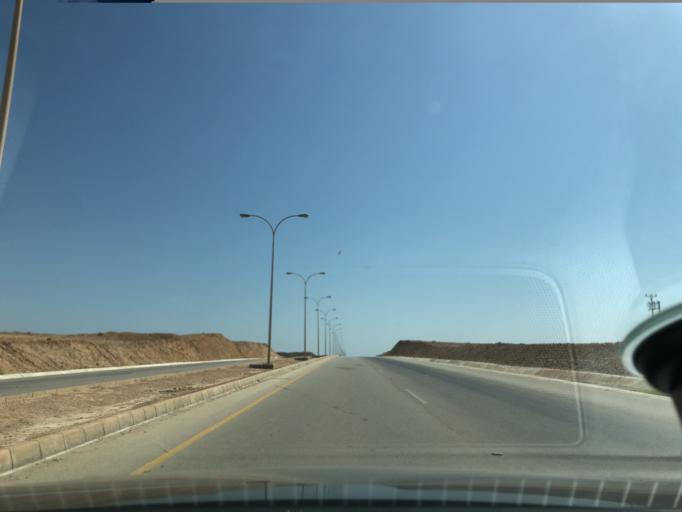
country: OM
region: Zufar
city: Salalah
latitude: 17.0448
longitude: 54.3354
